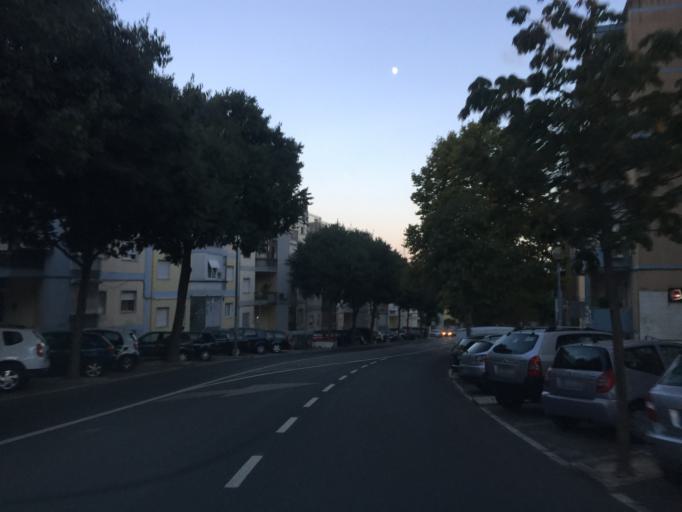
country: PT
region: Lisbon
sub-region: Odivelas
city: Odivelas
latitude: 38.7935
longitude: -9.1779
